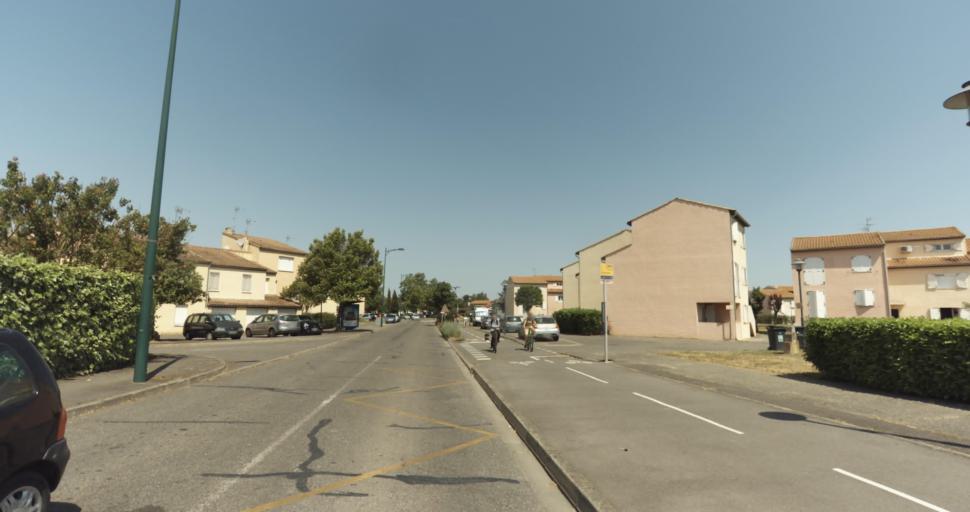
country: FR
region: Midi-Pyrenees
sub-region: Departement de la Haute-Garonne
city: Plaisance-du-Touch
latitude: 43.5613
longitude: 1.3051
